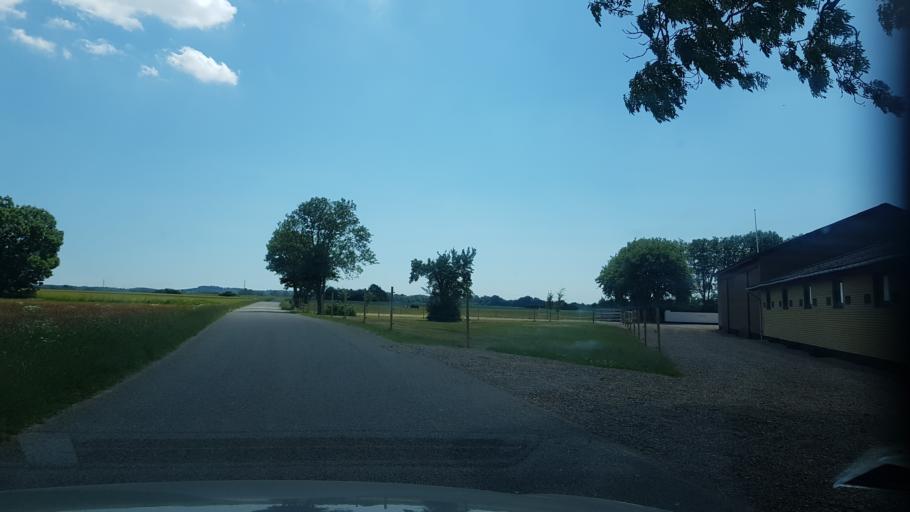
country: DK
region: Zealand
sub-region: Kalundborg Kommune
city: Svebolle
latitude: 55.6988
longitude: 11.2936
